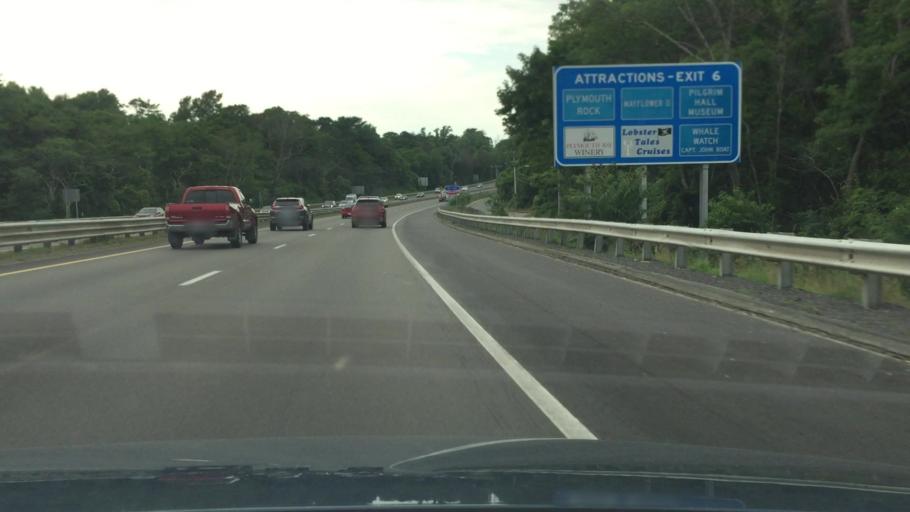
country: US
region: Massachusetts
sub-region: Plymouth County
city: Plymouth
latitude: 41.9450
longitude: -70.6757
